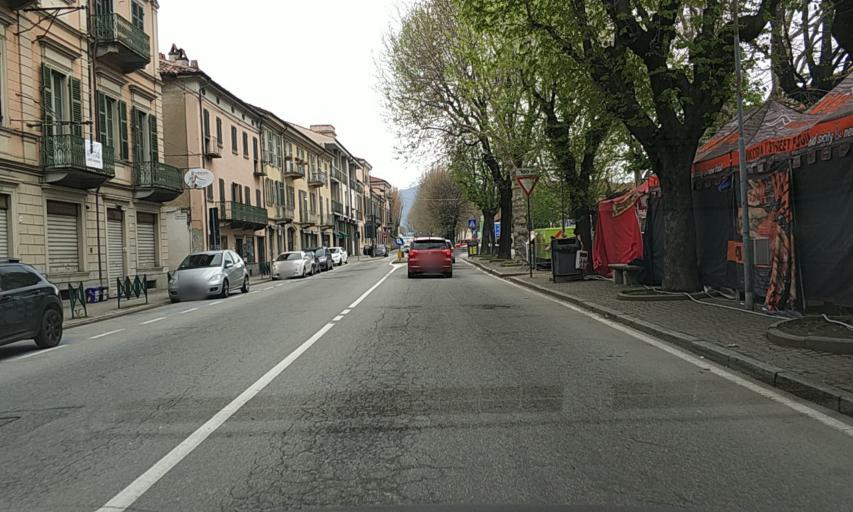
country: IT
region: Piedmont
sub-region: Provincia di Torino
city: Rivarolo Canavese
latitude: 45.3327
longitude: 7.7227
